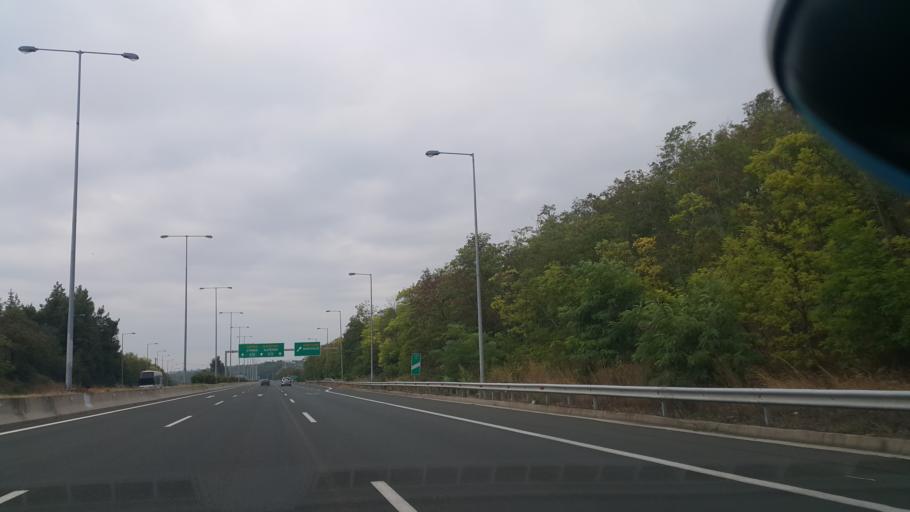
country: GR
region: Central Macedonia
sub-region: Nomos Pierias
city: Makrygialos
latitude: 40.4235
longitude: 22.5897
